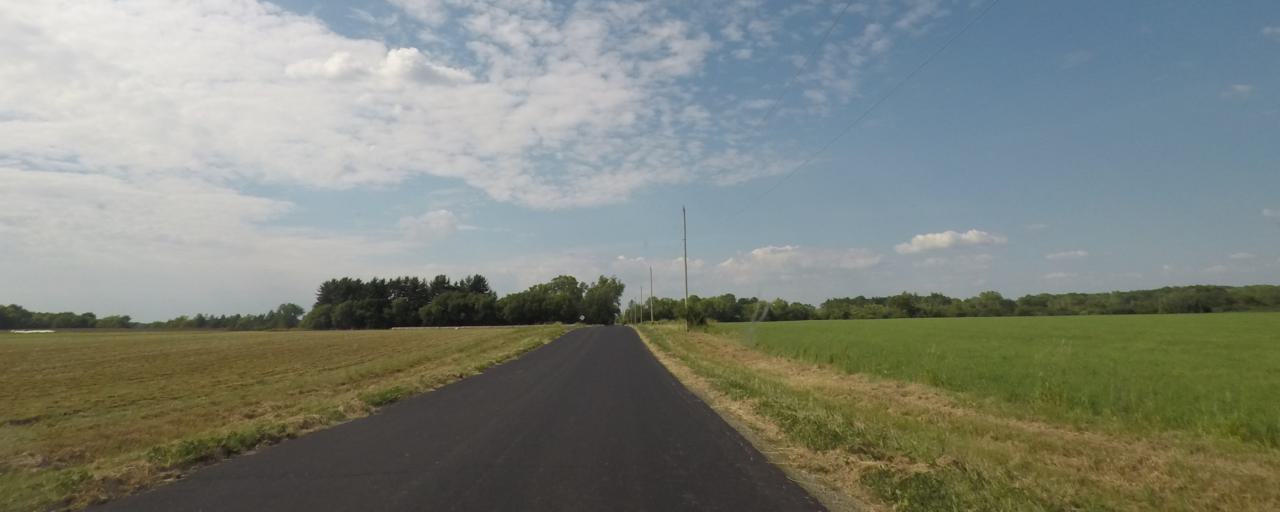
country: US
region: Wisconsin
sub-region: Walworth County
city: Elkhorn
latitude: 42.7792
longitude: -88.5294
